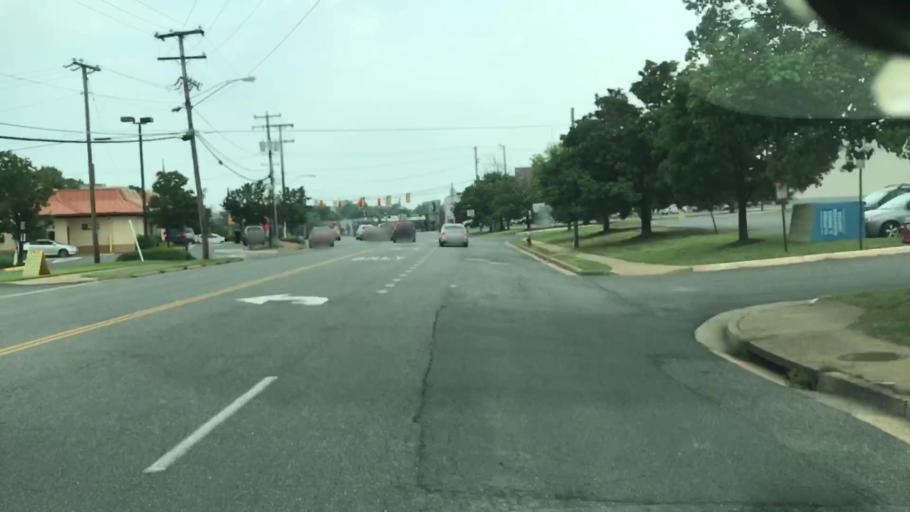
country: US
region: Virginia
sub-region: Fairfax County
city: Baileys Crossroads
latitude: 38.8470
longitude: -77.1252
